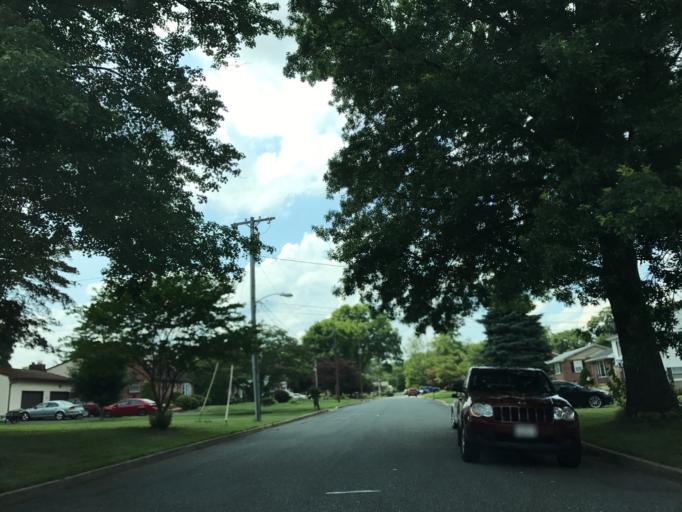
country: US
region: Maryland
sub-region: Harford County
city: North Bel Air
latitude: 39.5406
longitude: -76.3614
